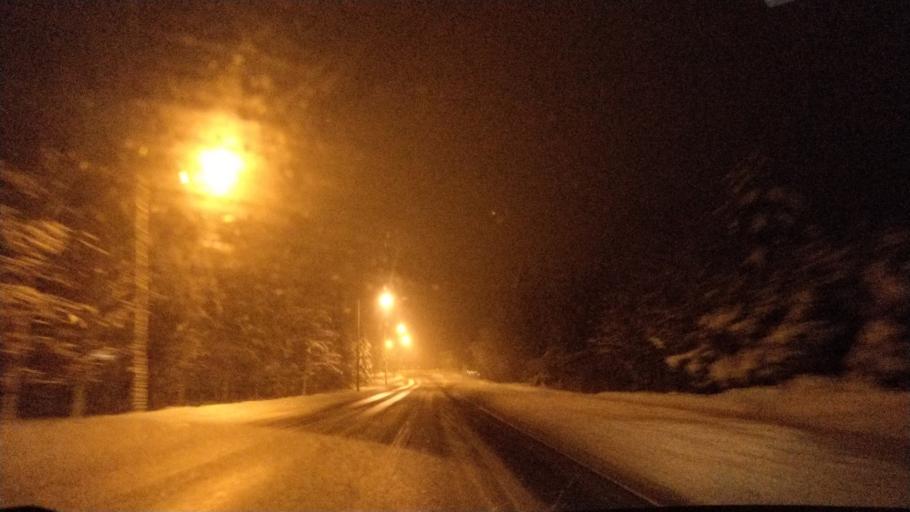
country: FI
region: Lapland
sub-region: Rovaniemi
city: Rovaniemi
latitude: 66.2767
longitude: 25.3318
